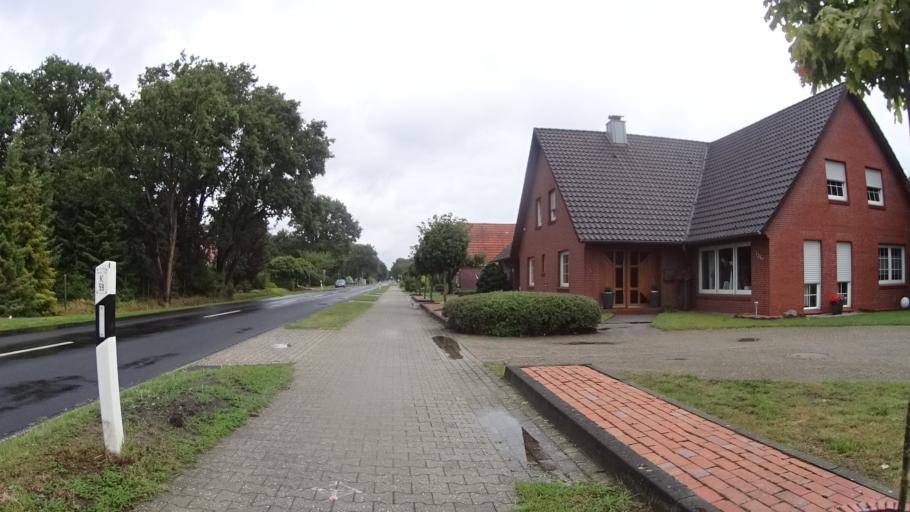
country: DE
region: Lower Saxony
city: Schwerinsdorf
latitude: 53.3442
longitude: 7.7085
